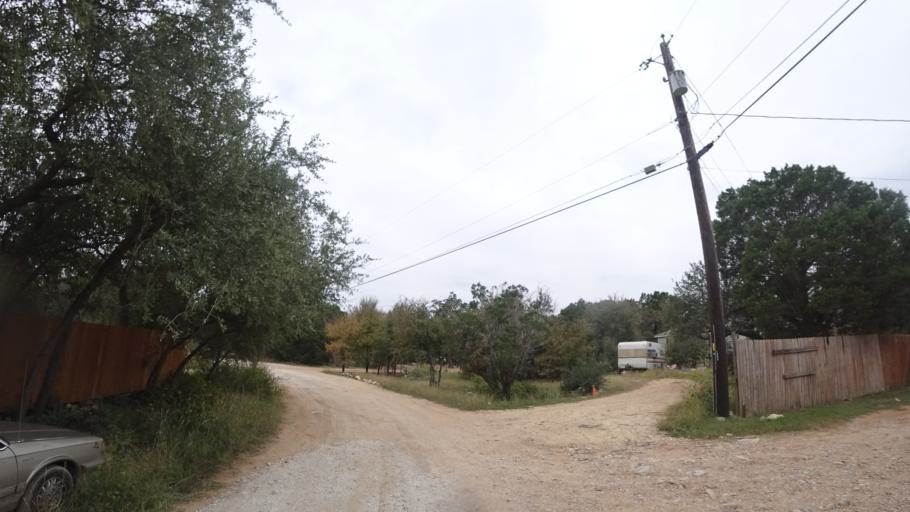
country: US
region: Texas
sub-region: Travis County
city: Hudson Bend
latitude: 30.3857
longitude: -97.9390
